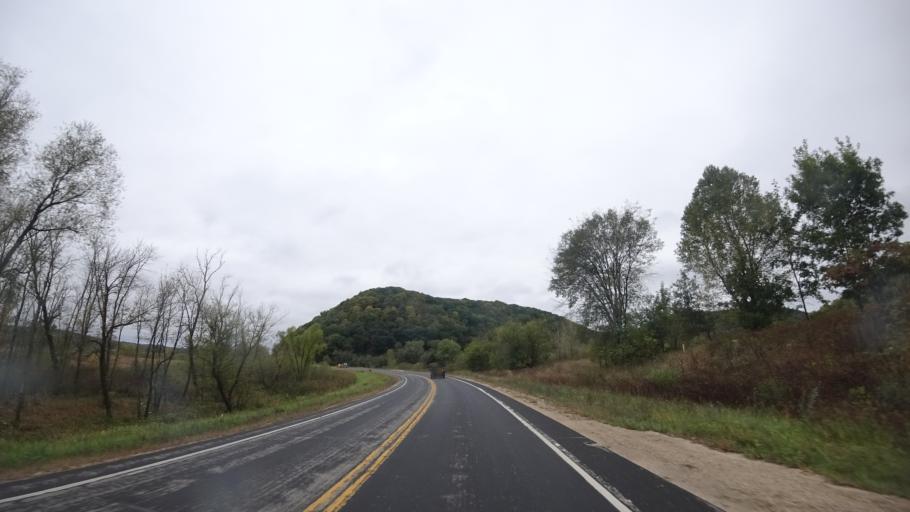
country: US
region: Wisconsin
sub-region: Grant County
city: Boscobel
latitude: 43.1270
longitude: -90.7676
